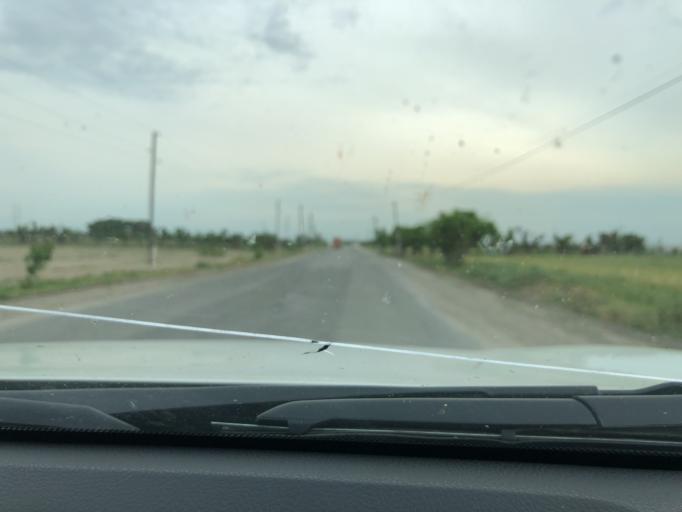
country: UZ
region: Toshkent
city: Bekobod
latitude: 40.1563
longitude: 69.2542
